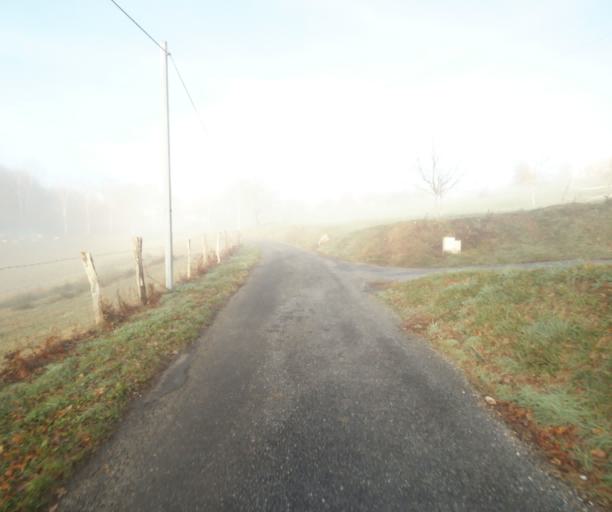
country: FR
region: Limousin
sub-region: Departement de la Correze
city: Tulle
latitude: 45.2632
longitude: 1.7825
